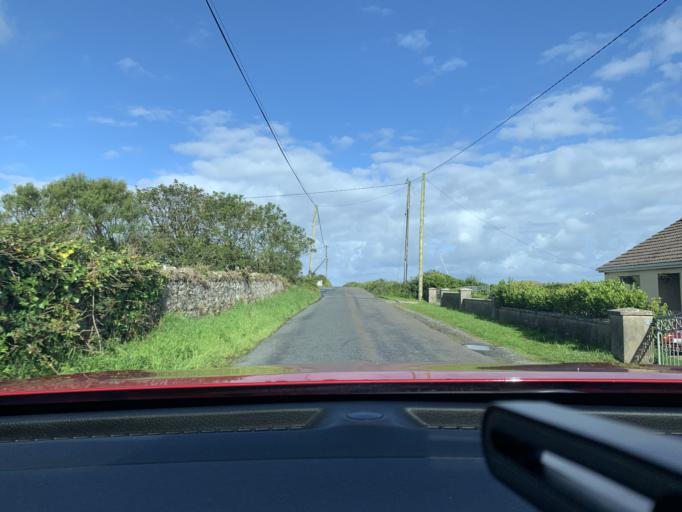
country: IE
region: Connaught
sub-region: Sligo
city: Strandhill
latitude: 54.3956
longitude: -8.5606
